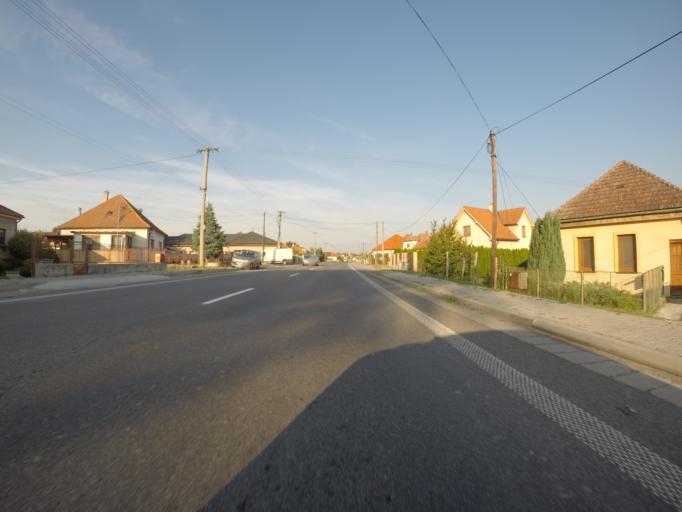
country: SK
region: Nitriansky
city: Banovce nad Bebravou
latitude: 48.5977
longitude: 18.2127
